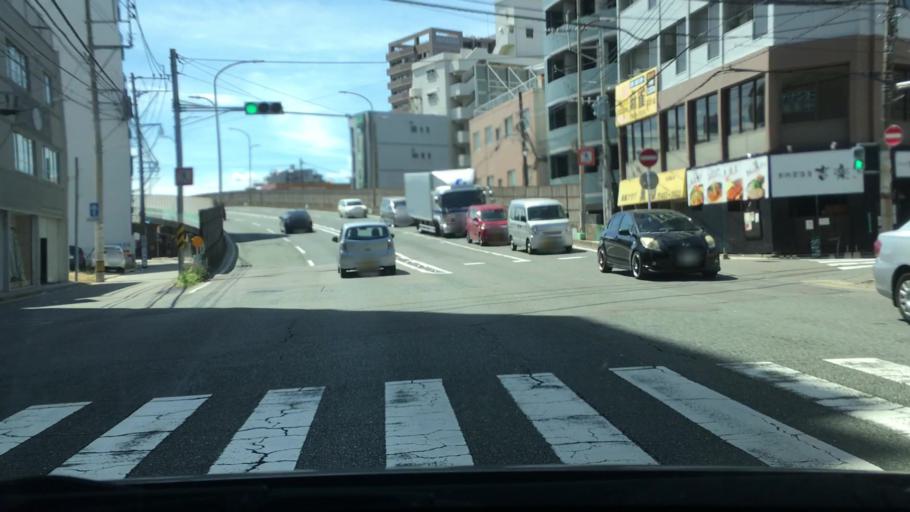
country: JP
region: Fukuoka
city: Fukuoka-shi
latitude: 33.5776
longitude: 130.4198
